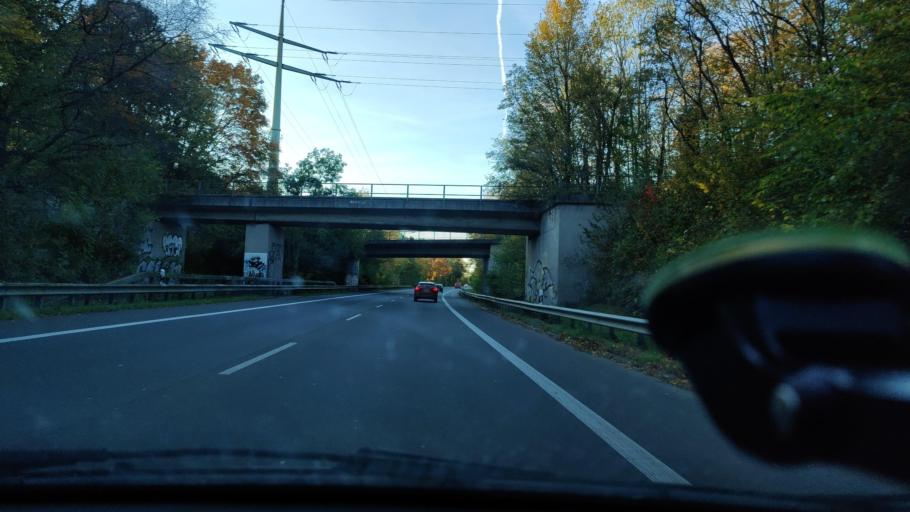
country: DE
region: North Rhine-Westphalia
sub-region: Regierungsbezirk Dusseldorf
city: Monchengladbach
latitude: 51.2289
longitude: 6.4675
